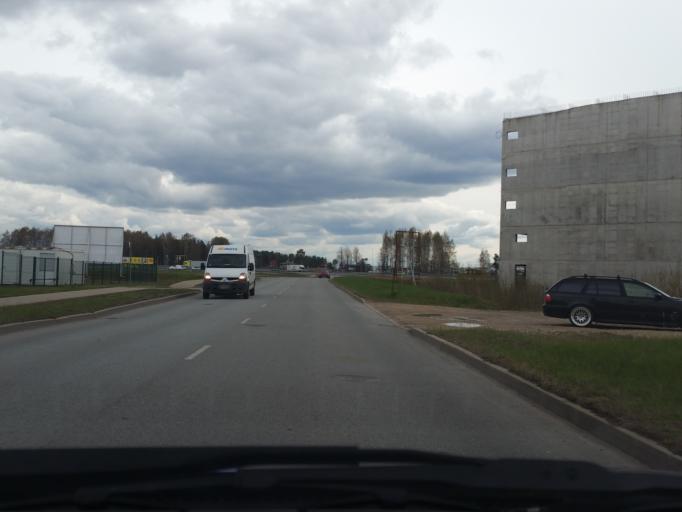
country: LV
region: Marupe
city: Marupe
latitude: 56.9247
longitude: 23.9927
